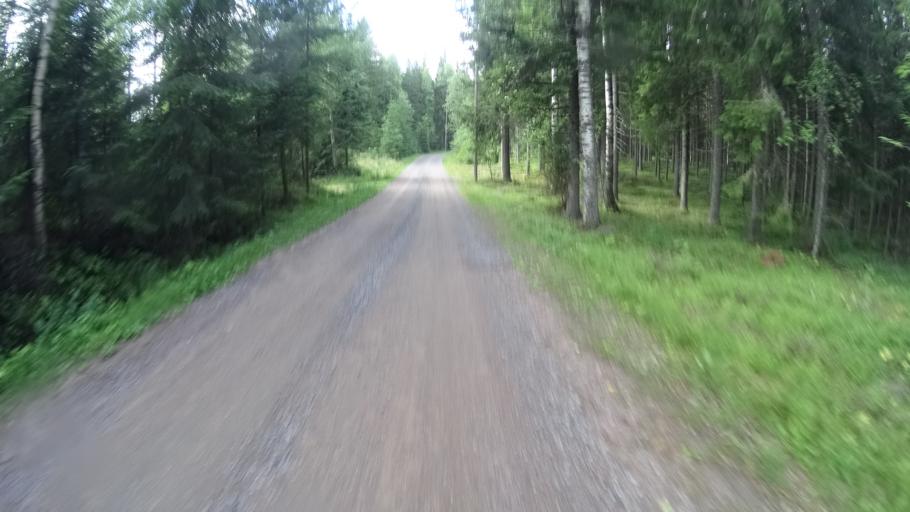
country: FI
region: Uusimaa
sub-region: Helsinki
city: Karkkila
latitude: 60.5987
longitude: 24.2154
